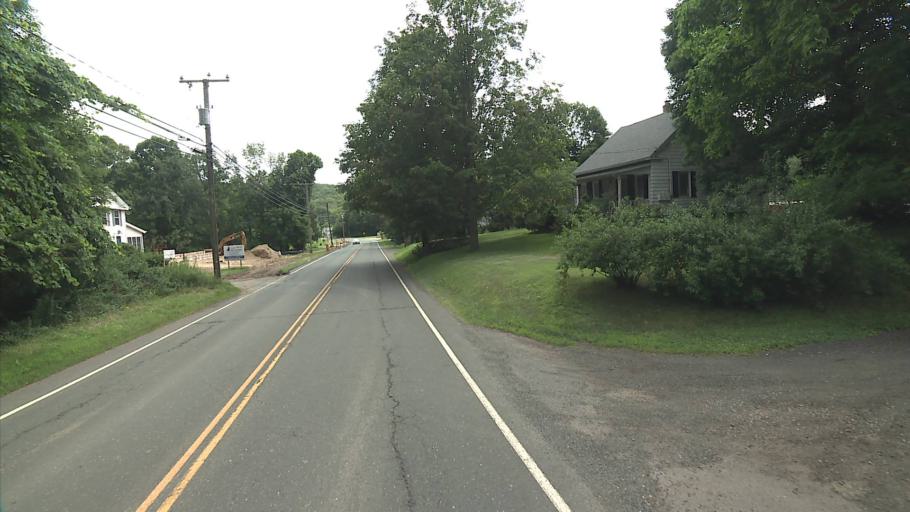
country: US
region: Connecticut
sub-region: New Haven County
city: Oxford
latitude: 41.4421
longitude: -73.1306
